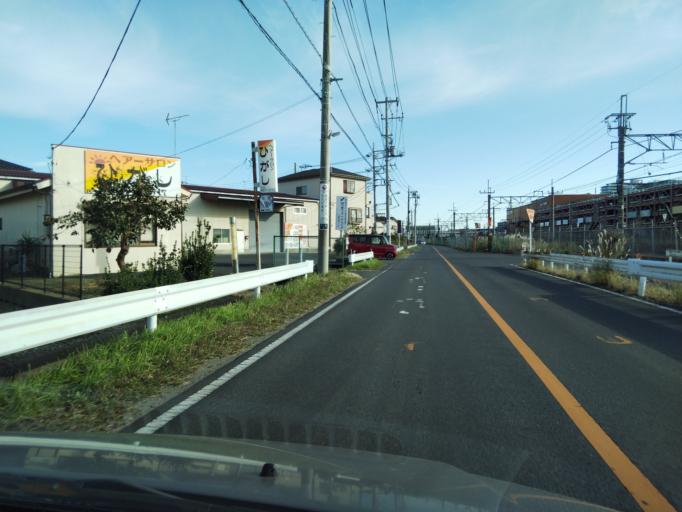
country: JP
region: Saitama
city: Yoshikawa
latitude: 35.8624
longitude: 139.8654
